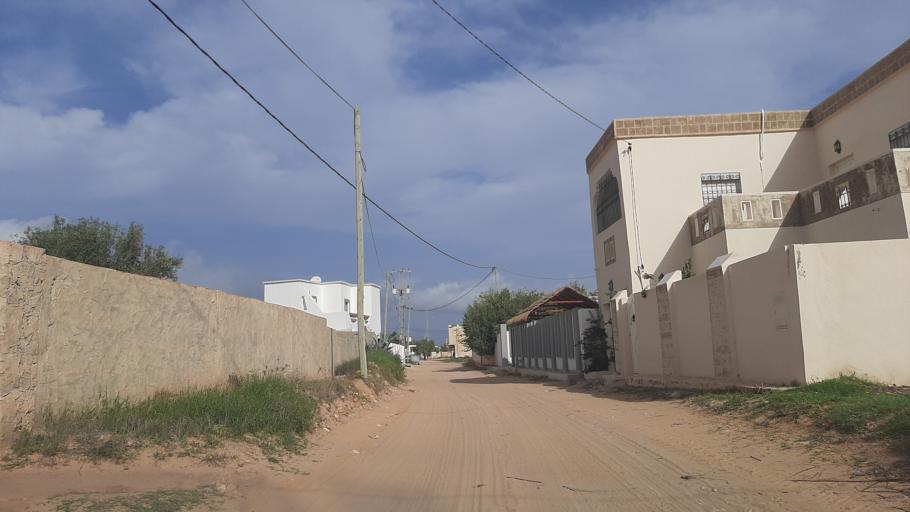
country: TN
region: Madanin
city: Midoun
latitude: 33.8127
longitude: 11.0256
